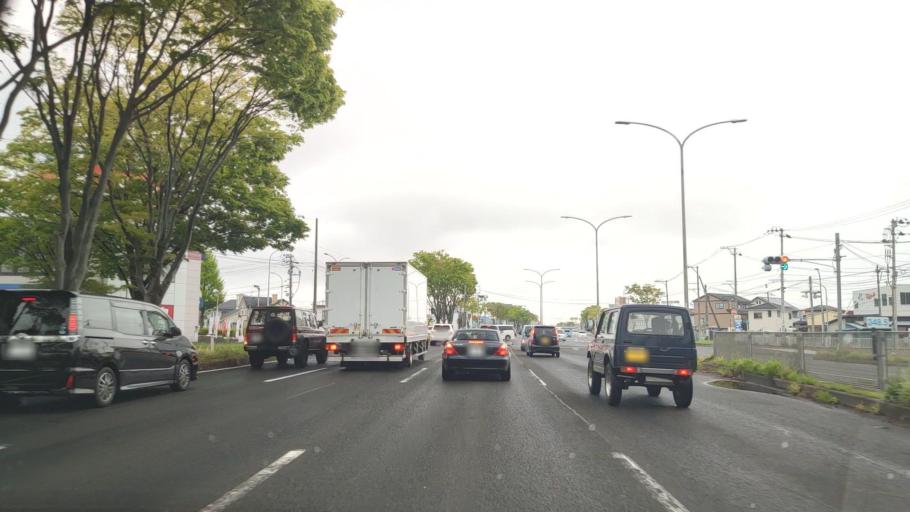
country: JP
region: Miyagi
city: Sendai
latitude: 38.2329
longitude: 140.9086
